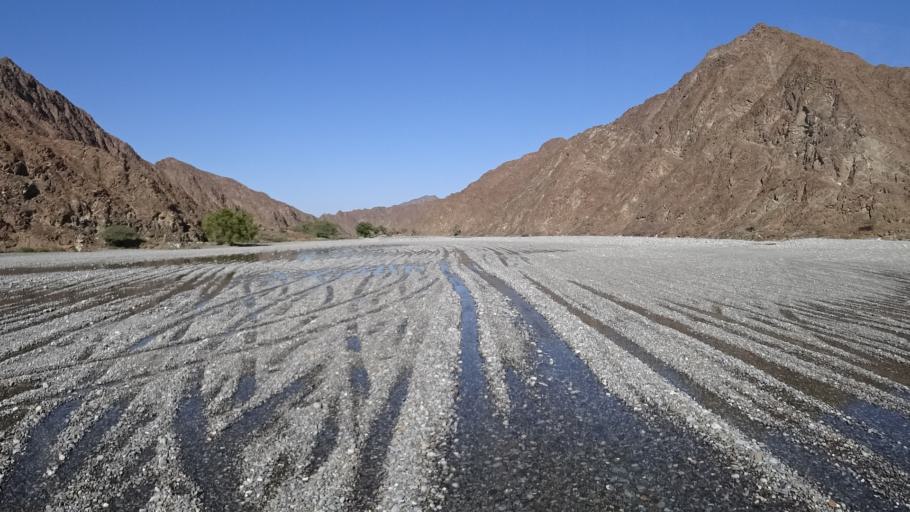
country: OM
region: Al Batinah
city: Bayt al `Awabi
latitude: 23.4006
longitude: 57.6655
